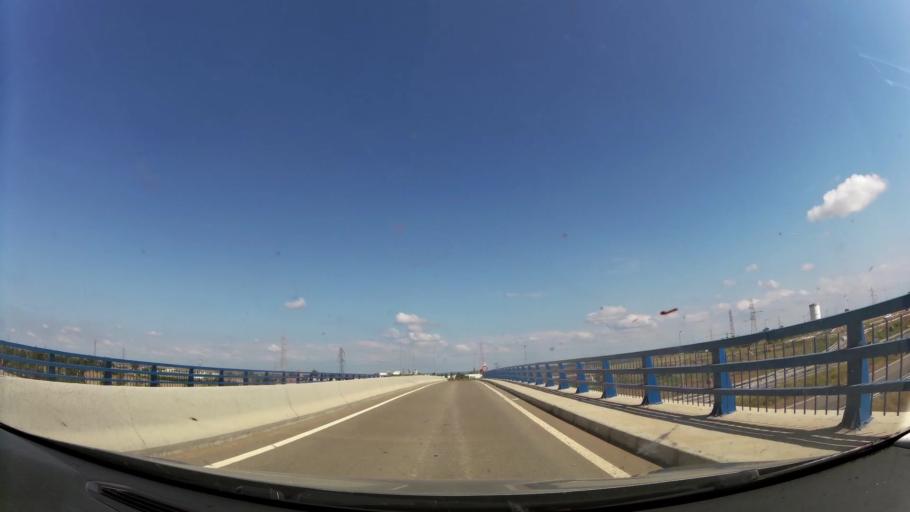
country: MA
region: Rabat-Sale-Zemmour-Zaer
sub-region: Rabat
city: Rabat
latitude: 33.9087
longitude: -6.7771
